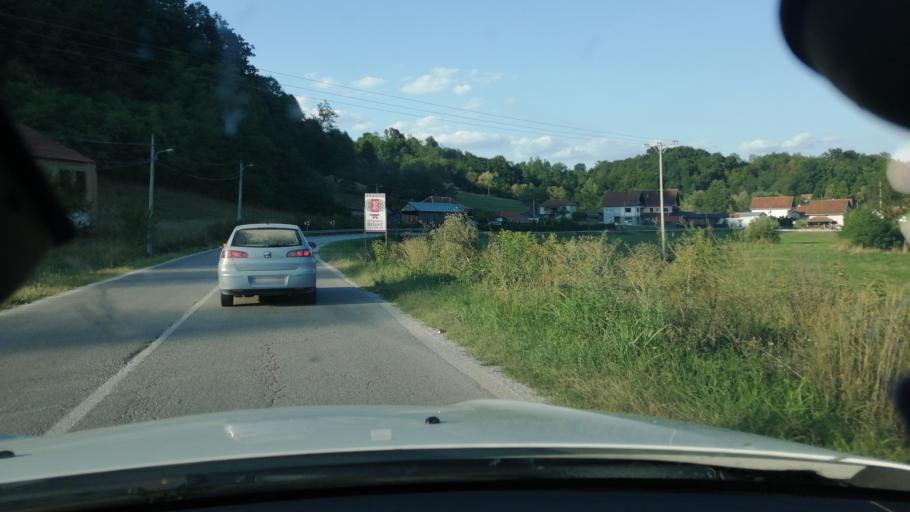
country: RS
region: Central Serbia
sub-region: Moravicki Okrug
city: Lucani
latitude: 43.7904
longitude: 20.2344
